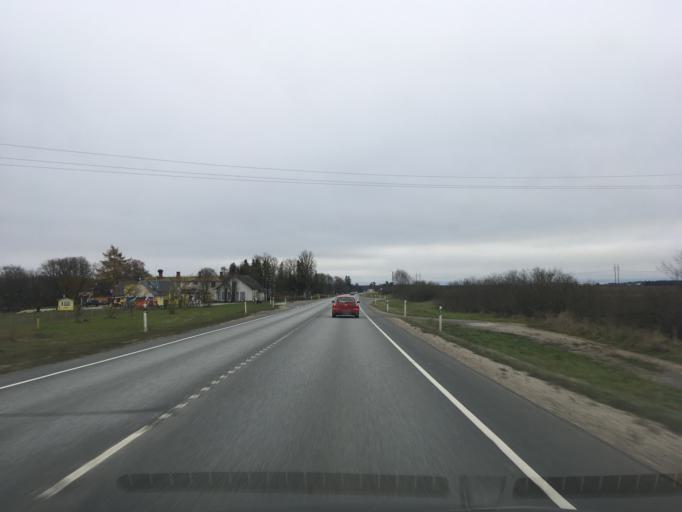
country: EE
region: Laeaene-Virumaa
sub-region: Someru vald
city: Someru
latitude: 59.3802
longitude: 26.4129
